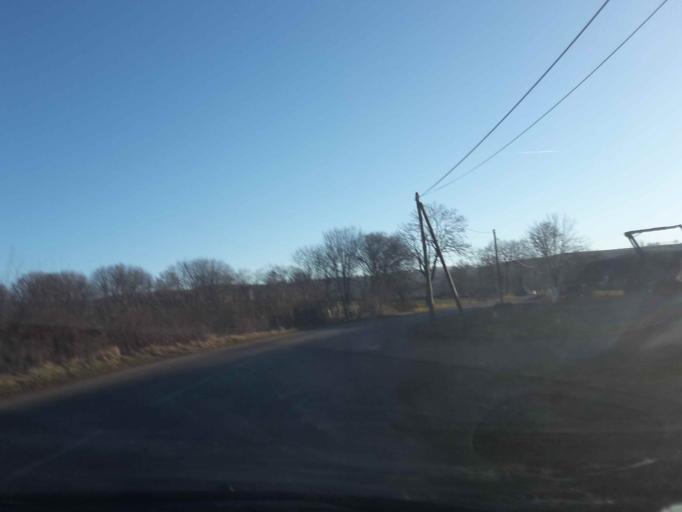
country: FR
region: Auvergne
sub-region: Departement du Cantal
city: Ydes
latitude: 45.2461
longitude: 2.5411
